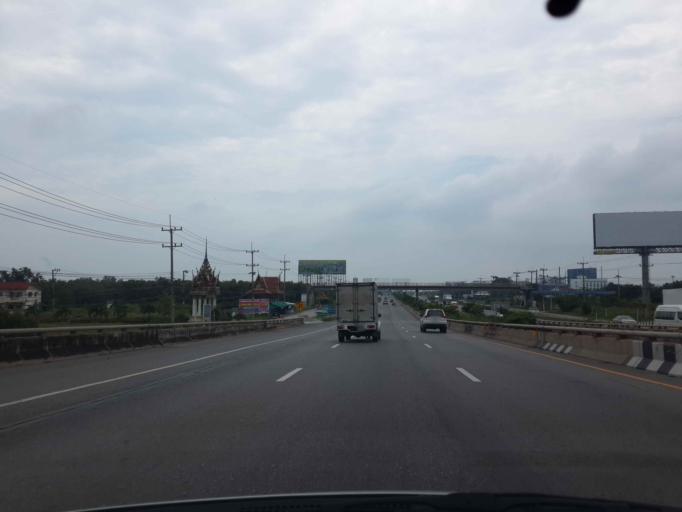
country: TH
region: Samut Sakhon
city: Ban Phaeo
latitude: 13.4843
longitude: 100.1204
